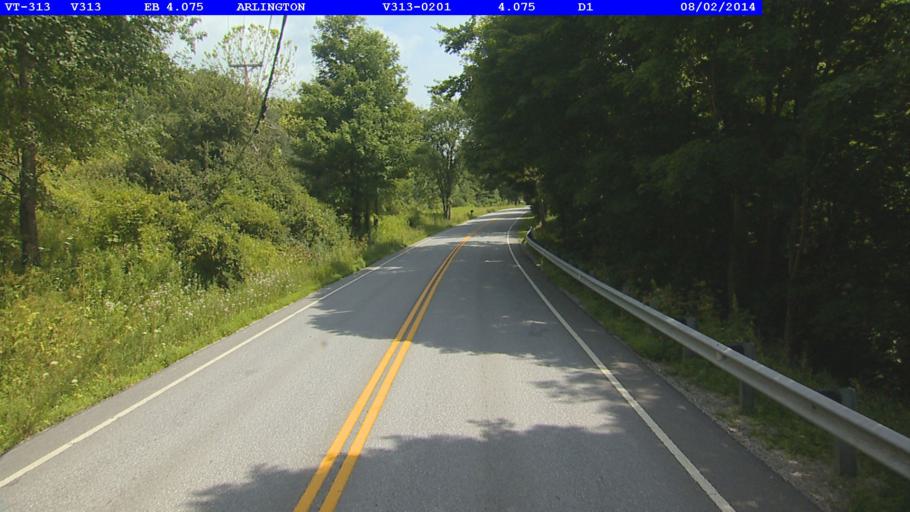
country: US
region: Vermont
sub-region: Bennington County
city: Arlington
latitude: 43.0904
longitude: -73.1959
